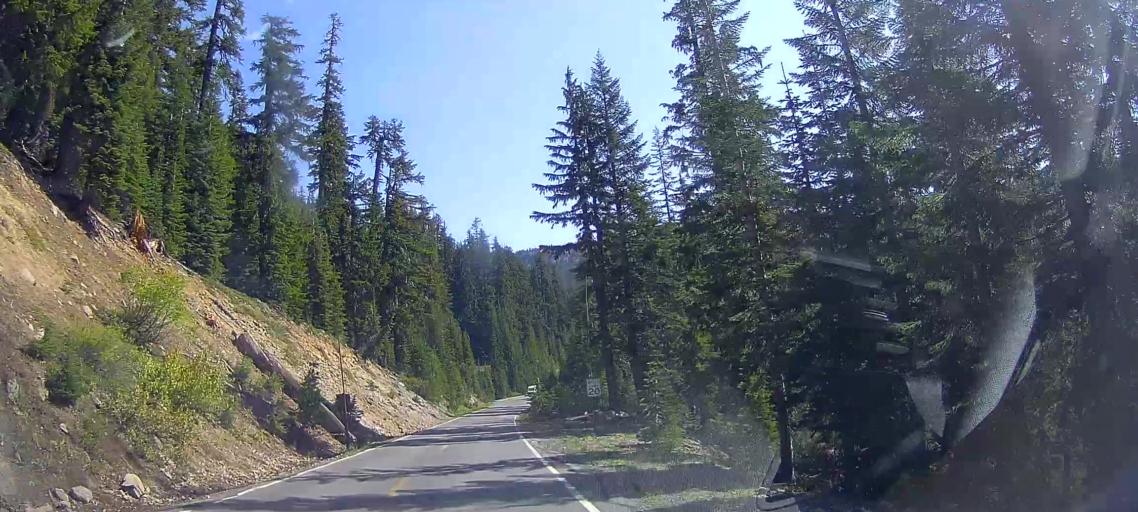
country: US
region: Oregon
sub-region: Klamath County
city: Klamath Falls
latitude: 42.8830
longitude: -122.1005
